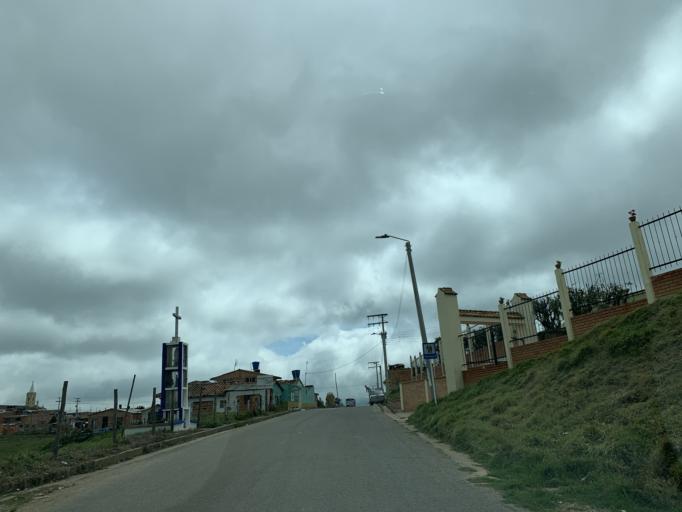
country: CO
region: Boyaca
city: Tunja
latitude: 5.5795
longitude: -73.3655
